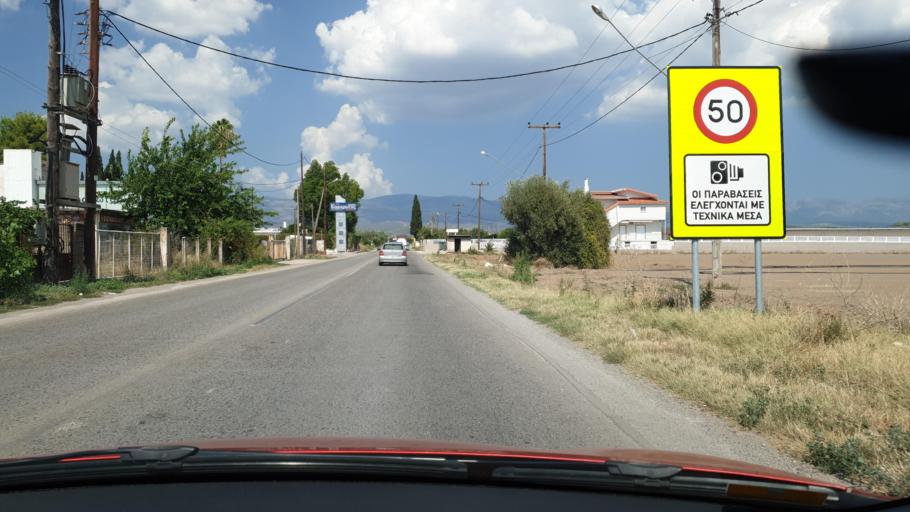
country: GR
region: Central Greece
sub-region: Nomos Evvoias
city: Kastella
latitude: 38.5471
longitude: 23.6287
